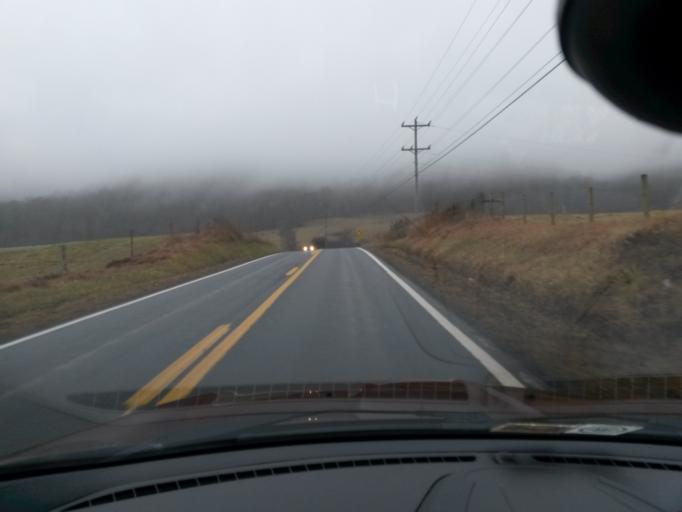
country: US
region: West Virginia
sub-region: Greenbrier County
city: Lewisburg
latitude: 37.8753
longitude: -80.5261
